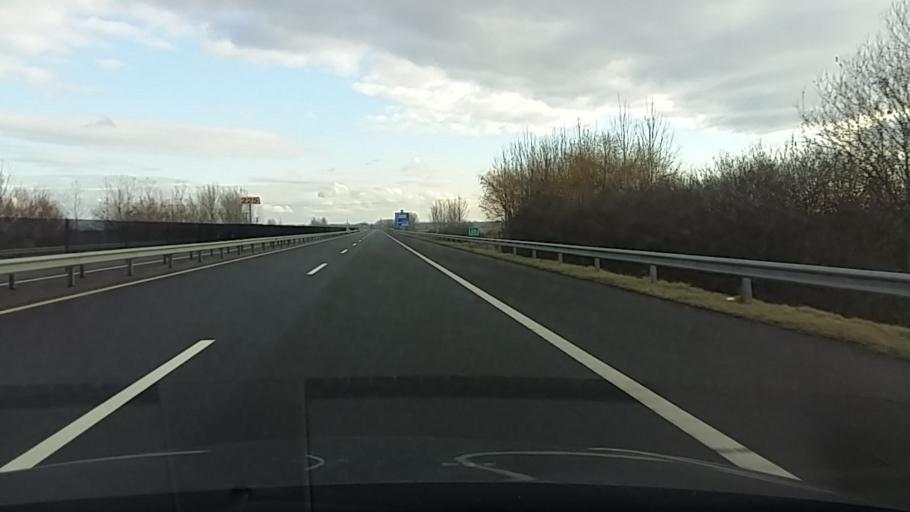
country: HU
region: Szabolcs-Szatmar-Bereg
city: Nyiregyhaza
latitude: 47.8906
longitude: 21.6913
